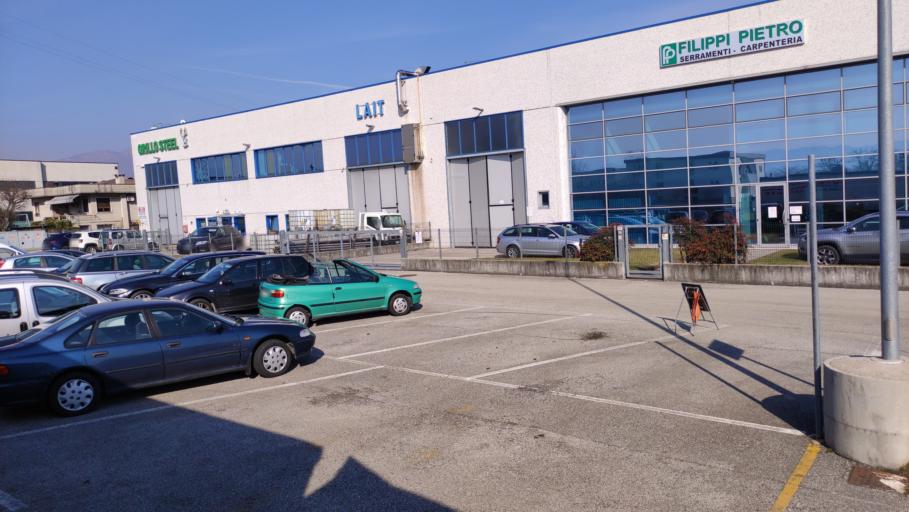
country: IT
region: Veneto
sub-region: Provincia di Vicenza
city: Thiene
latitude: 45.6815
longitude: 11.4745
